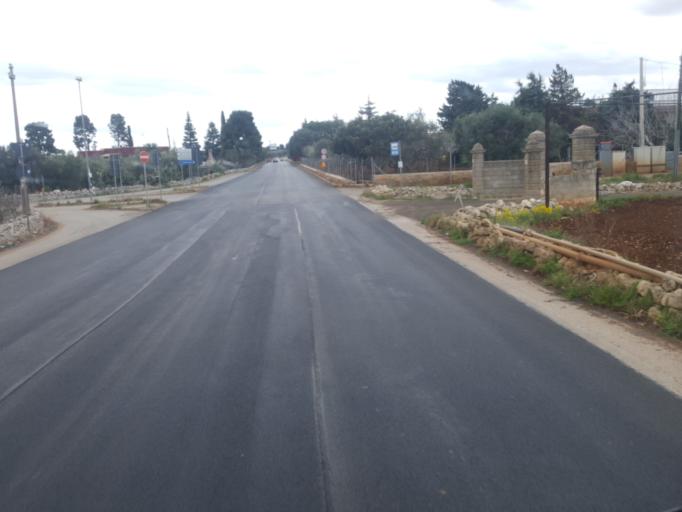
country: IT
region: Apulia
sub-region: Provincia di Bari
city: Conversano
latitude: 41.0062
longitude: 17.1338
